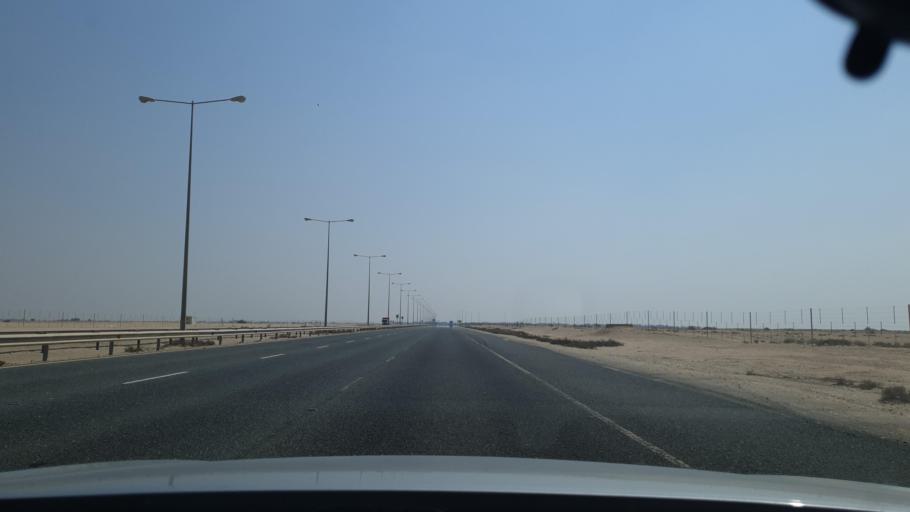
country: QA
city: Al Ghuwayriyah
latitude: 25.8023
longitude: 51.3813
